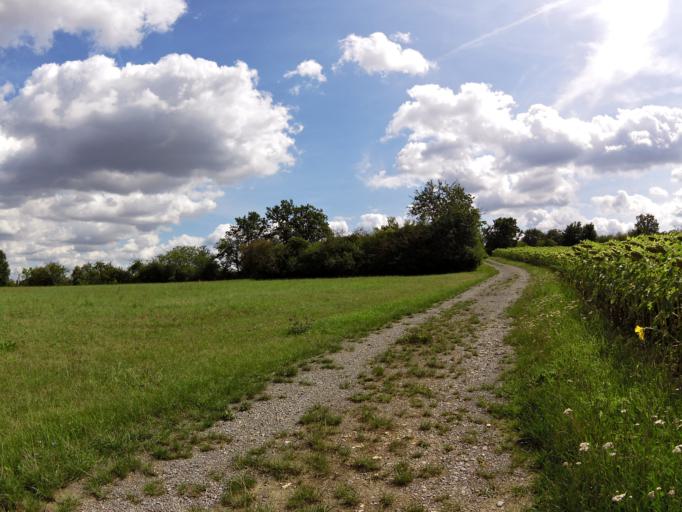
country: DE
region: Bavaria
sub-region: Regierungsbezirk Unterfranken
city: Margetshochheim
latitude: 49.8421
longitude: 9.8471
